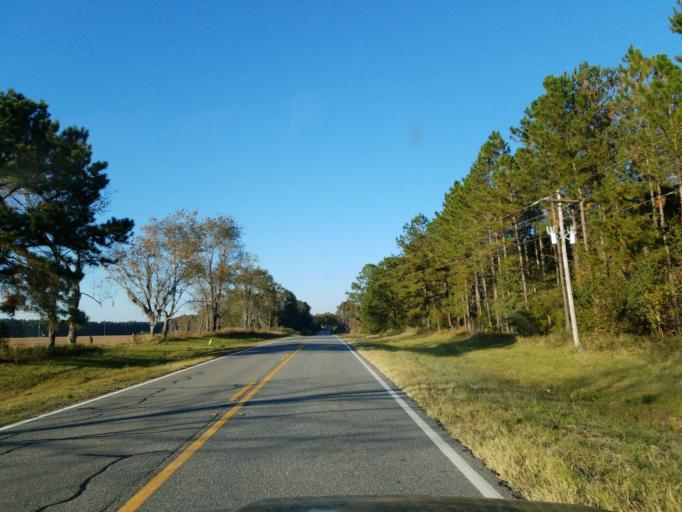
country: US
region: Georgia
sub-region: Lanier County
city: Lakeland
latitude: 30.9652
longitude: -83.0821
